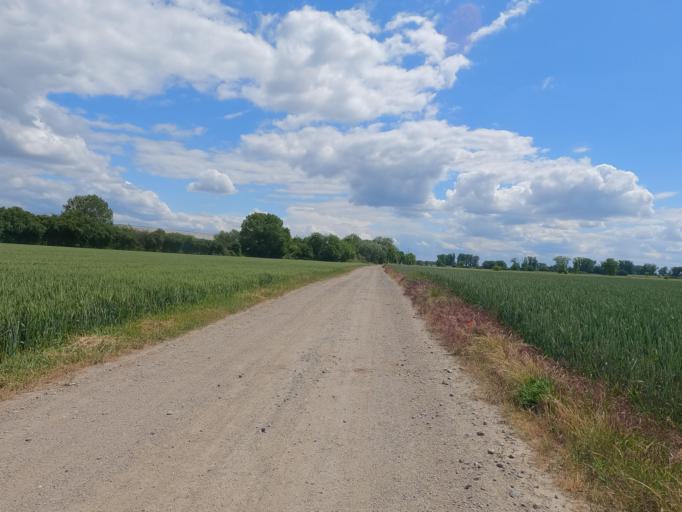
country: DE
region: Rheinland-Pfalz
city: Eich
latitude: 49.7091
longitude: 8.4064
